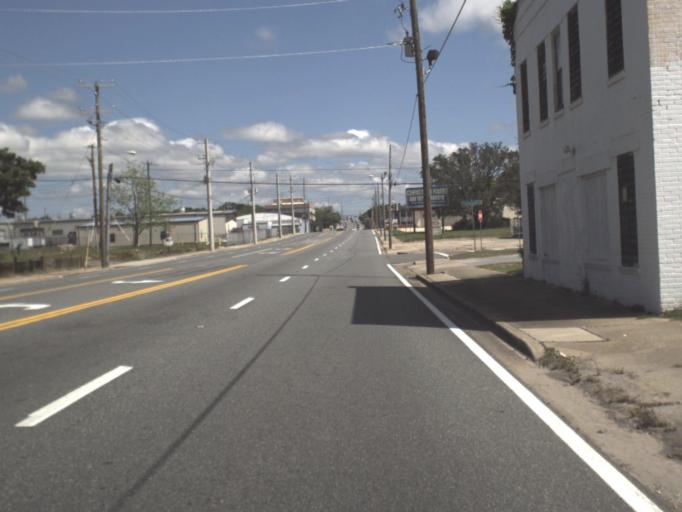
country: US
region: Florida
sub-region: Escambia County
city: Pensacola
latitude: 30.4085
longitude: -87.2419
